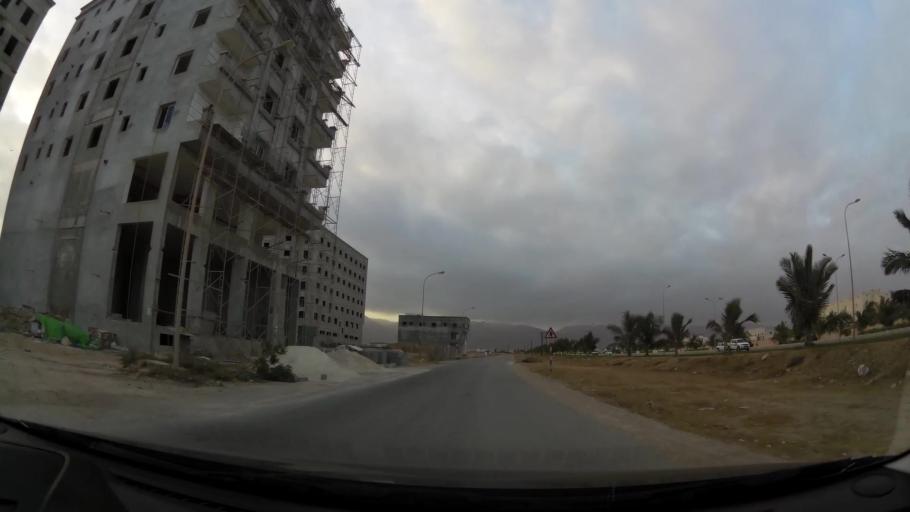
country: OM
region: Zufar
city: Salalah
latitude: 17.0259
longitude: 54.0317
